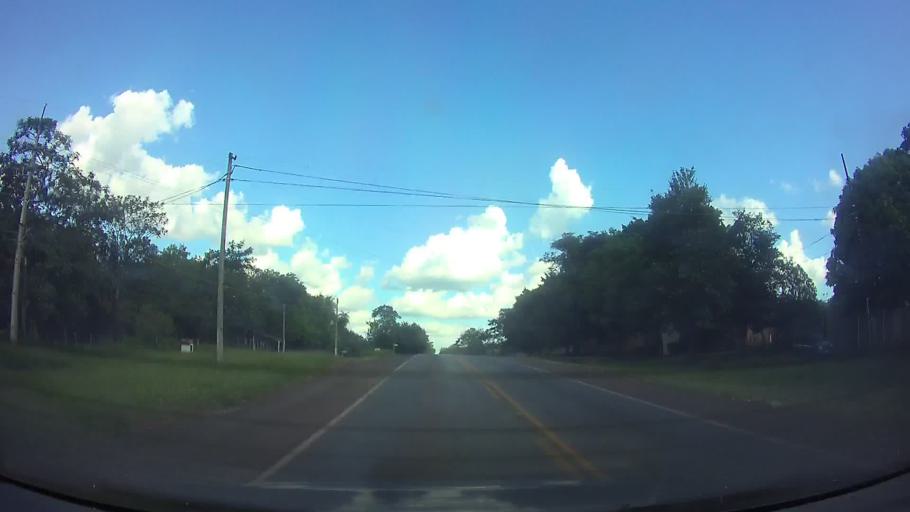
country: PY
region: Cordillera
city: Eusebio Ayala
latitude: -25.4074
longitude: -56.9402
